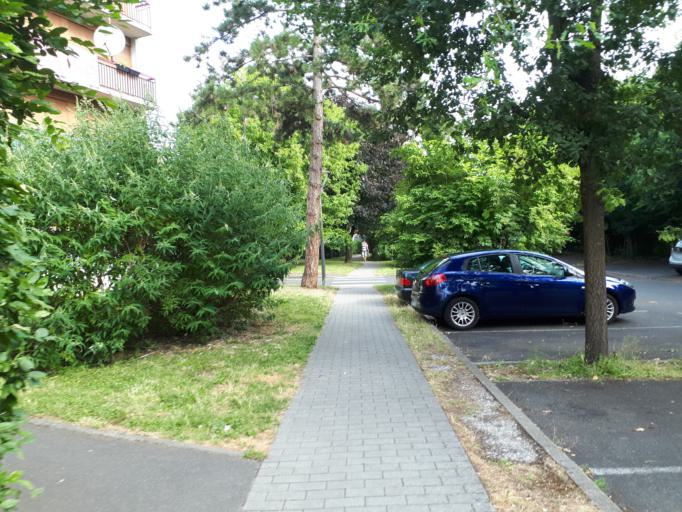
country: FR
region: Centre
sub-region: Departement d'Indre-et-Loire
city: Tours
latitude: 47.3819
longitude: 0.7010
